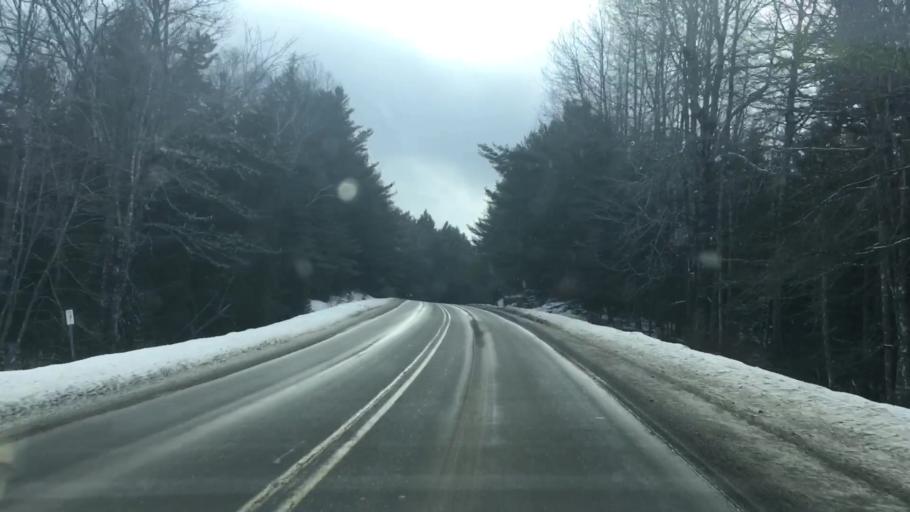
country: US
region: Maine
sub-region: Washington County
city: Calais
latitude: 45.0451
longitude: -67.3277
